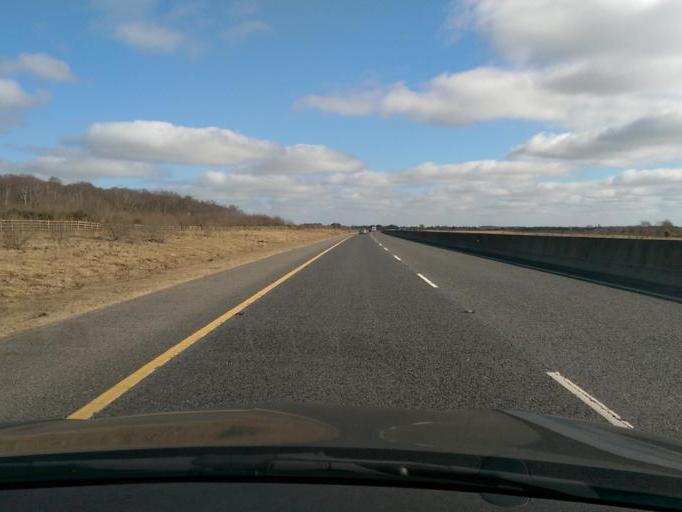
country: IE
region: Leinster
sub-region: An Iarmhi
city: Rochfortbridge
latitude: 53.4189
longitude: -7.2540
